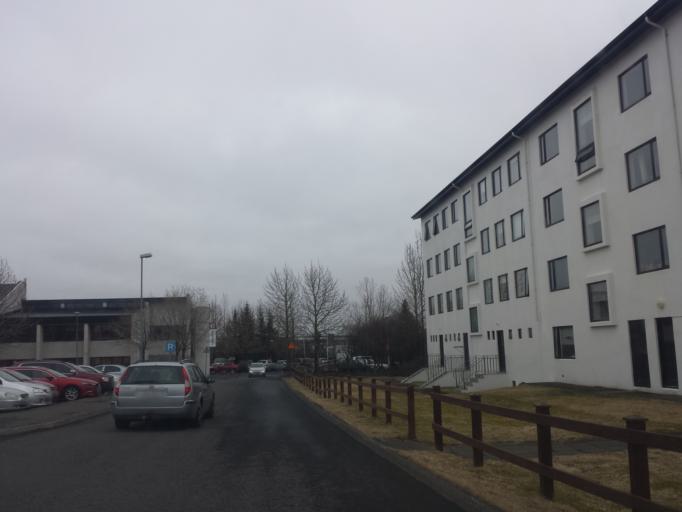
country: IS
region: Capital Region
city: Reykjavik
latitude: 64.1043
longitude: -21.8166
